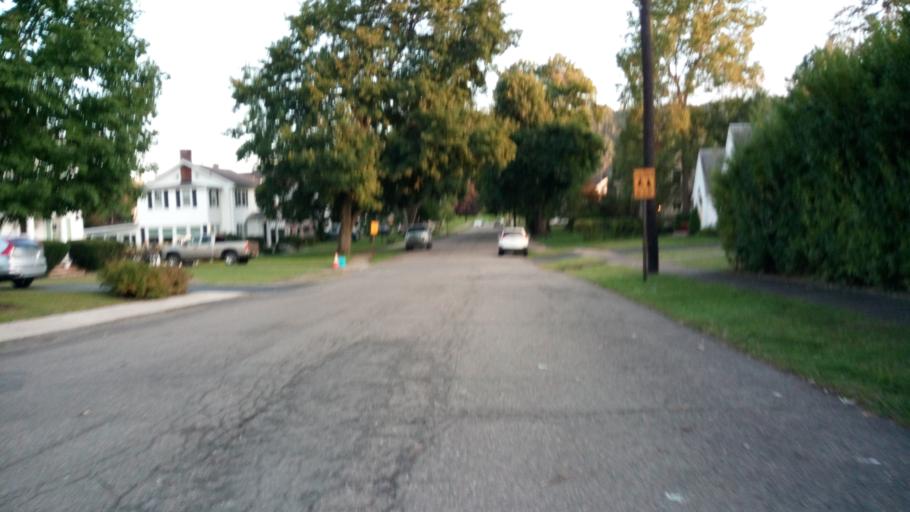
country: US
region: New York
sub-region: Chemung County
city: West Elmira
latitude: 42.0795
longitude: -76.8337
